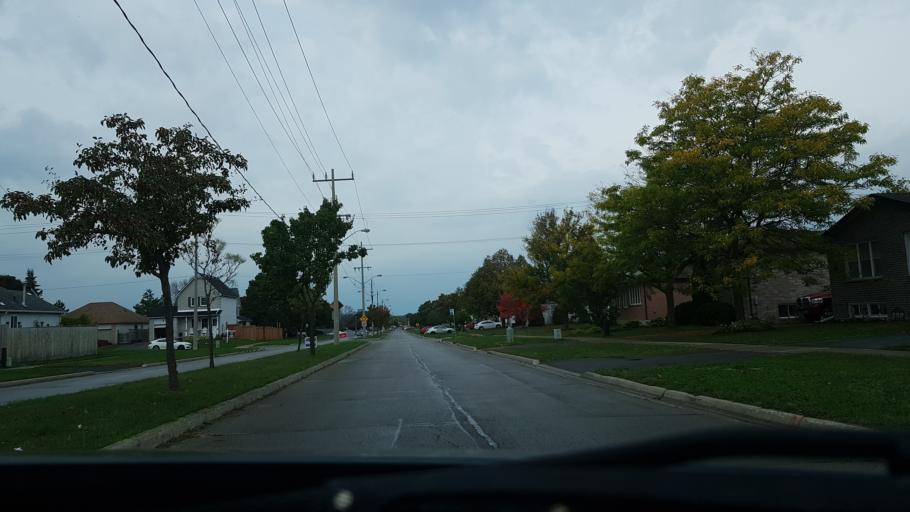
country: CA
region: Ontario
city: Omemee
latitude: 44.3661
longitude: -78.7464
